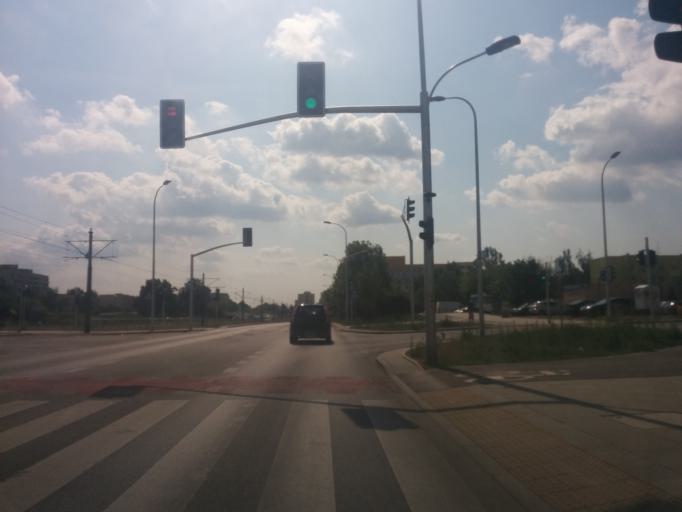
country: PL
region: Masovian Voivodeship
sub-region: Warszawa
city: Bialoleka
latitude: 52.3210
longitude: 20.9472
